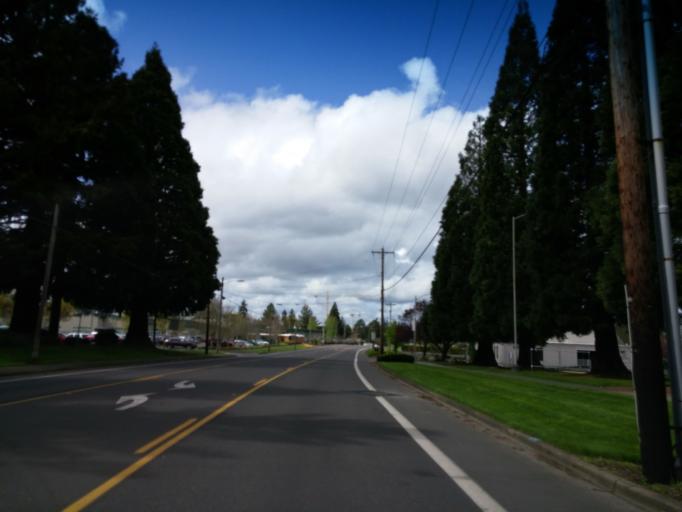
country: US
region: Oregon
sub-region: Washington County
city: Cedar Hills
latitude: 45.5053
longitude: -122.8159
